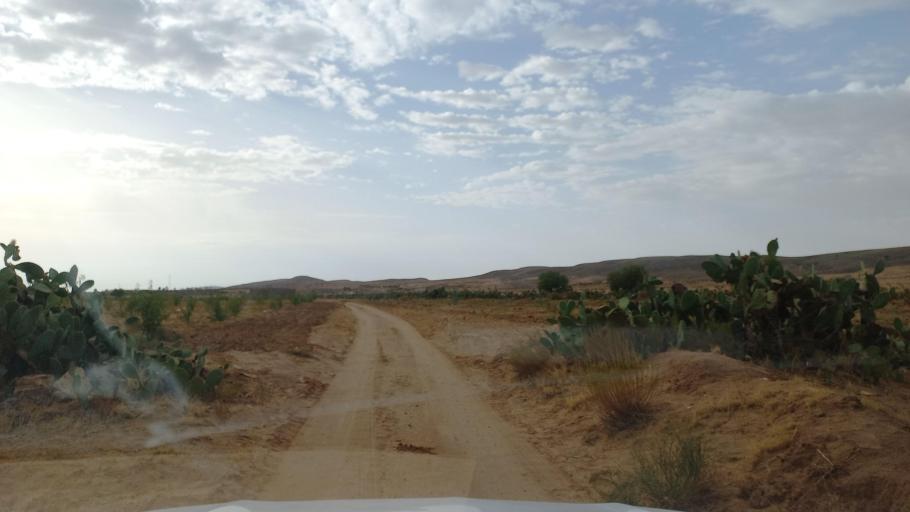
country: TN
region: Al Qasrayn
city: Kasserine
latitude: 35.1892
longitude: 9.0518
